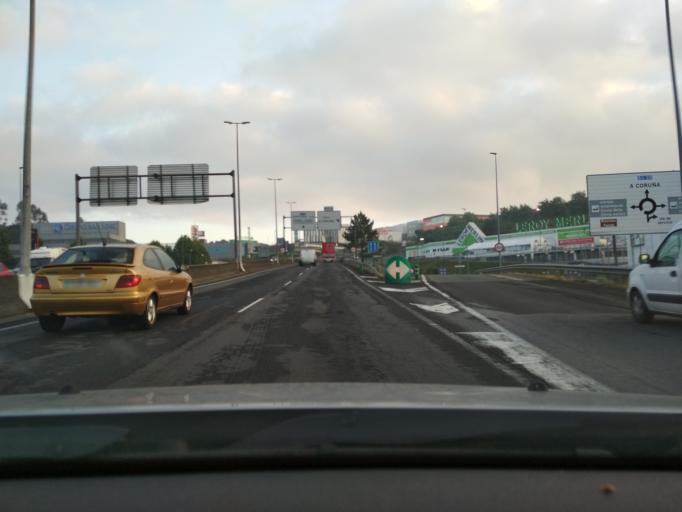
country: ES
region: Galicia
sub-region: Provincia da Coruna
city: Santiago de Compostela
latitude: 42.9012
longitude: -8.5109
